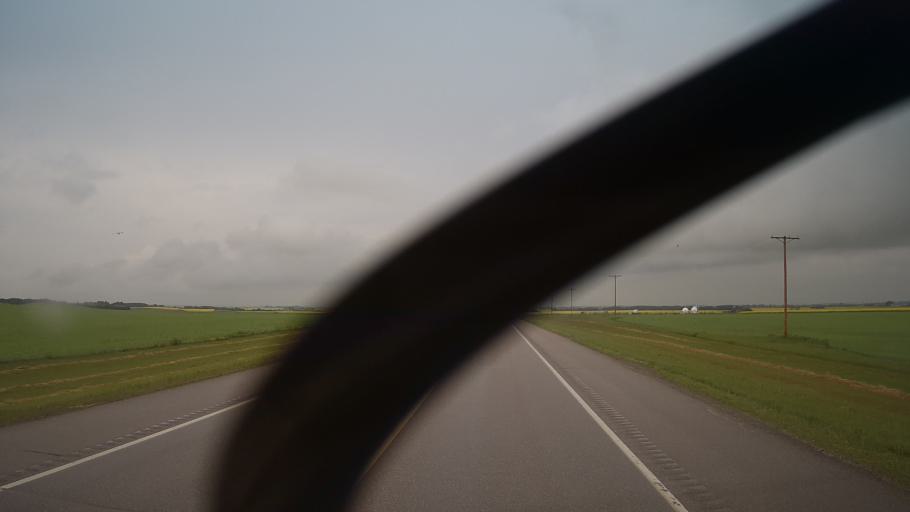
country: CA
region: Saskatchewan
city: Wilkie
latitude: 52.4179
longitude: -108.8891
